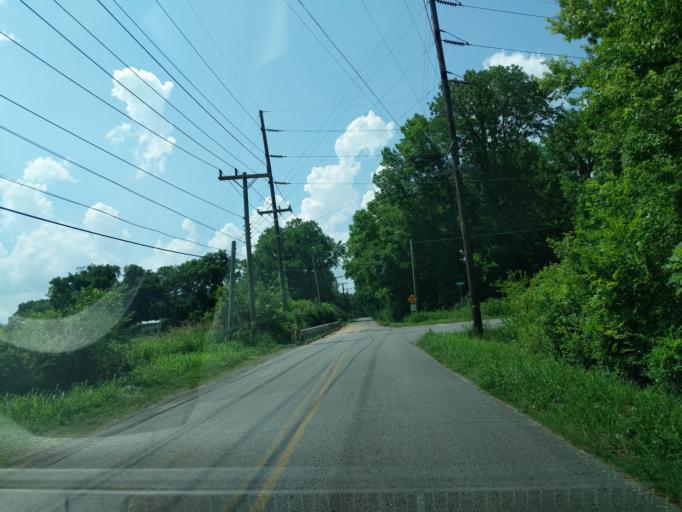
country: US
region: Tennessee
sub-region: Davidson County
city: Goodlettsville
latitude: 36.2822
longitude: -86.6756
